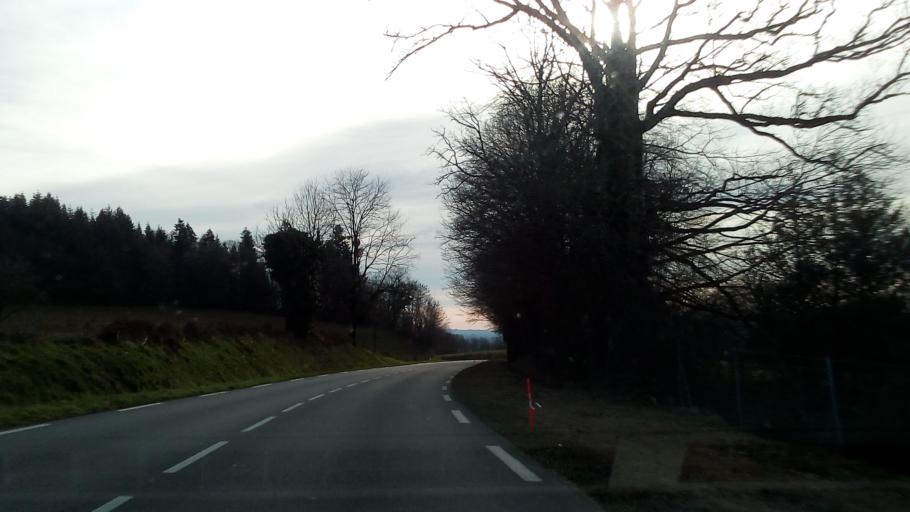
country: FR
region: Limousin
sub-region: Departement de la Correze
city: Naves
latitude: 45.3331
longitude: 1.7611
